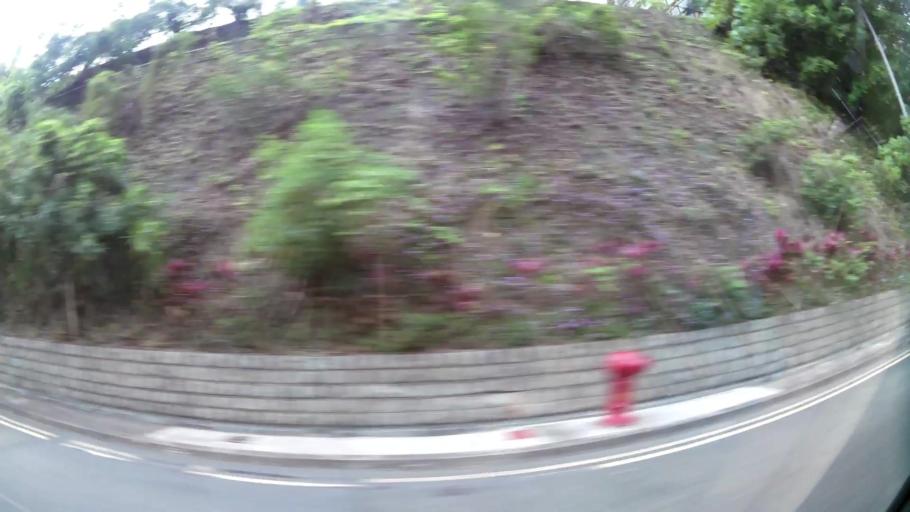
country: HK
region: Kowloon City
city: Kowloon
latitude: 22.3101
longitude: 114.1781
